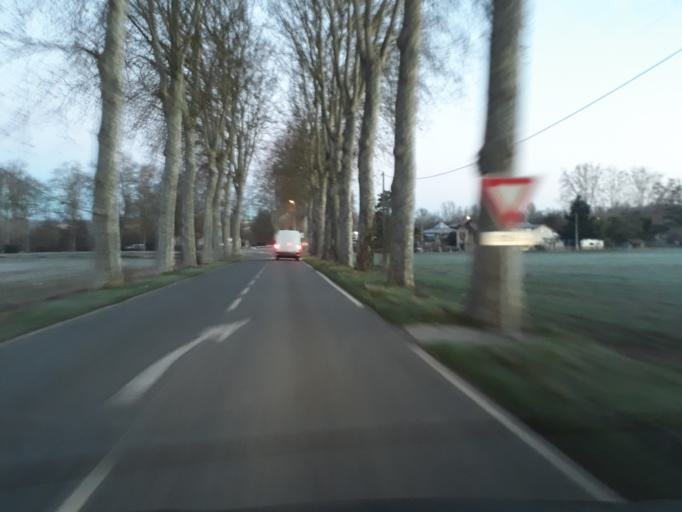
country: FR
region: Midi-Pyrenees
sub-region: Departement du Gers
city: Samatan
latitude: 43.4855
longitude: 0.9353
